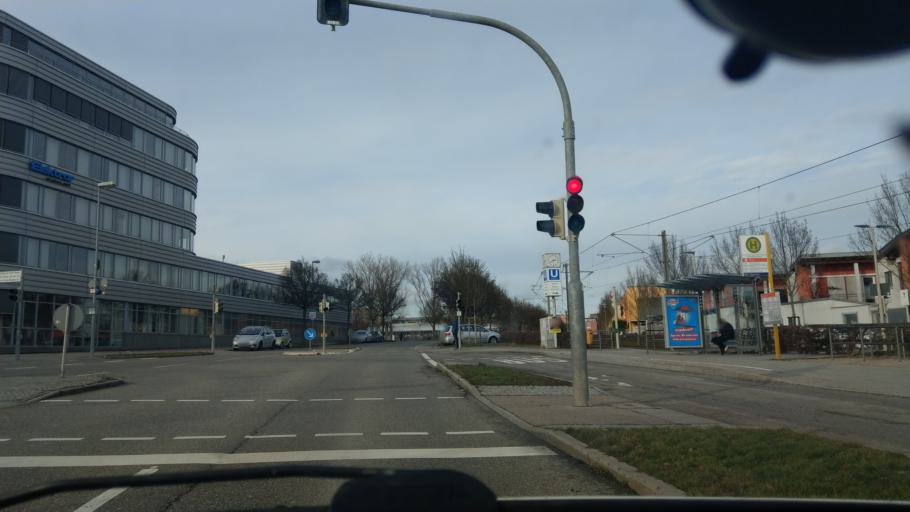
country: DE
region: Baden-Wuerttemberg
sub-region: Regierungsbezirk Stuttgart
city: Ostfildern
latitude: 48.7152
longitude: 9.2727
